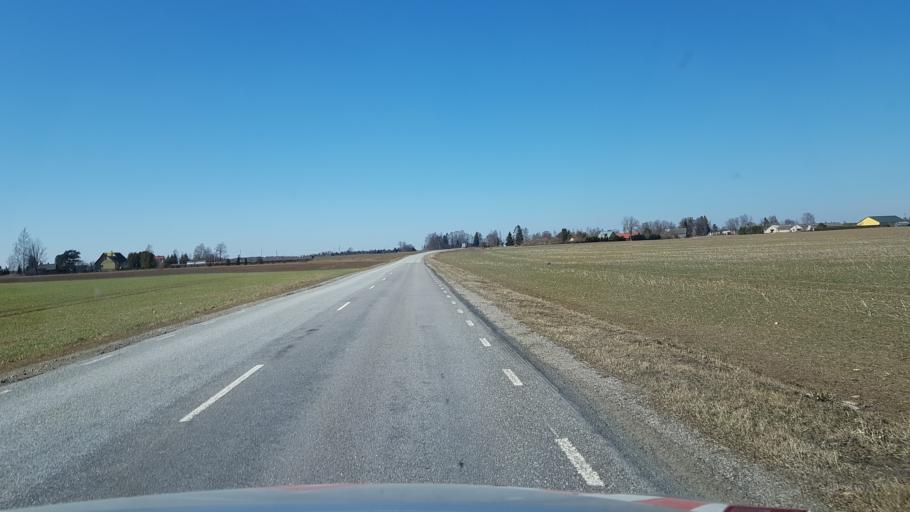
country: EE
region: Laeaene-Virumaa
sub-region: Vaeike-Maarja vald
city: Vaike-Maarja
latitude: 59.1399
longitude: 26.2407
